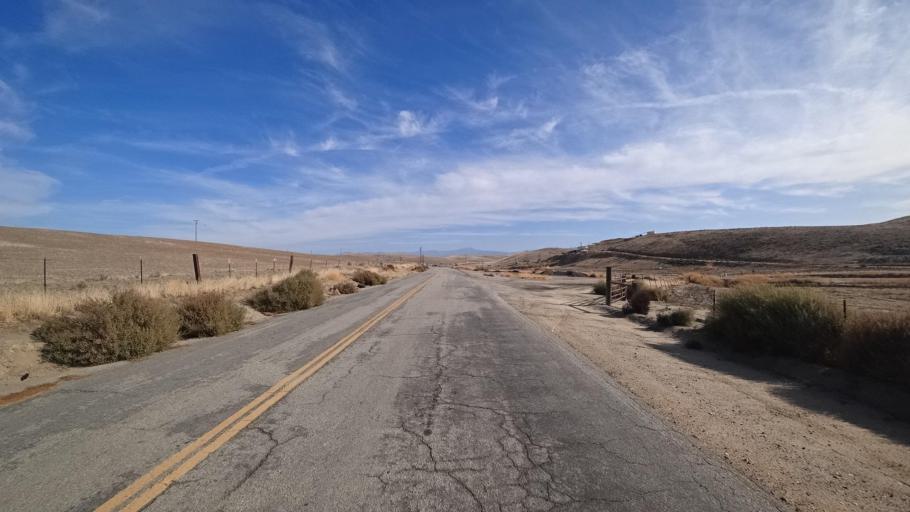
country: US
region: California
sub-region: Kern County
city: Oildale
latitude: 35.6062
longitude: -118.9502
